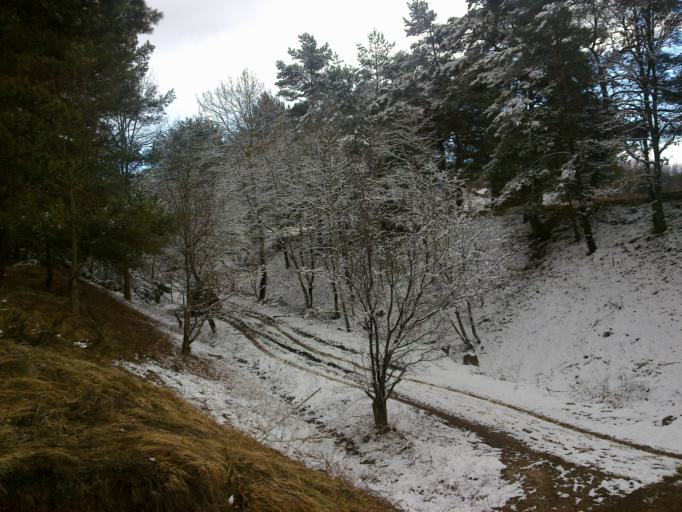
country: PL
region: Pomeranian Voivodeship
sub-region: Powiat gdanski
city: Kowale
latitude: 54.3538
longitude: 18.5506
